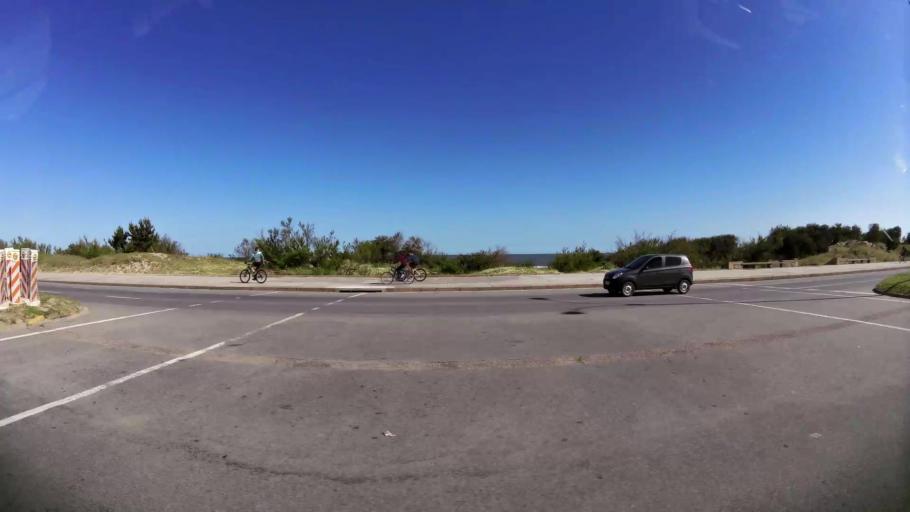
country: UY
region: Canelones
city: Barra de Carrasco
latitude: -34.8875
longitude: -56.0471
